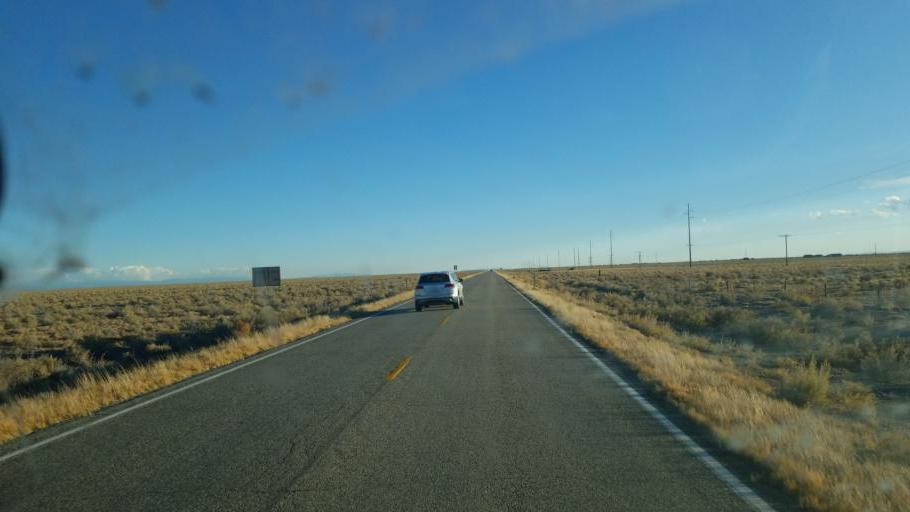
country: US
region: Colorado
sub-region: Saguache County
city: Center
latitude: 37.8595
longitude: -105.8930
